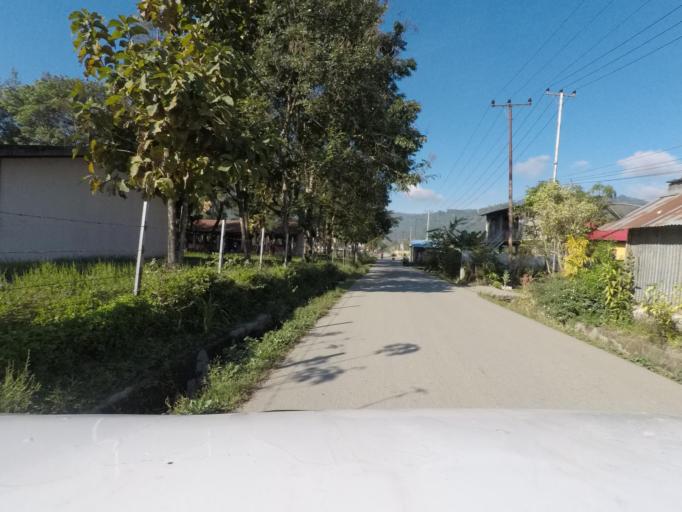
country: TL
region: Ermera
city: Gleno
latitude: -8.7221
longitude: 125.4318
